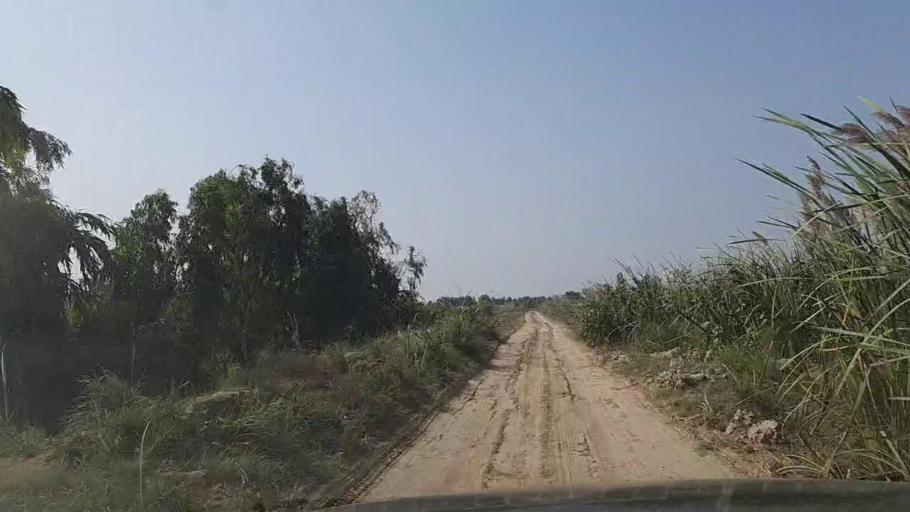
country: PK
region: Sindh
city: Gharo
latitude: 24.7236
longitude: 67.6836
